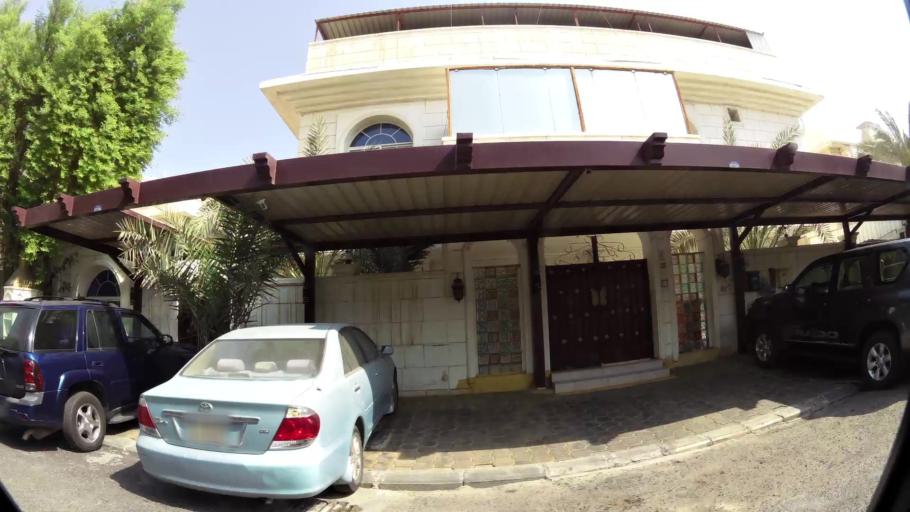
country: KW
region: Al Asimah
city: Ad Dasmah
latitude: 29.3592
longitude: 48.0147
